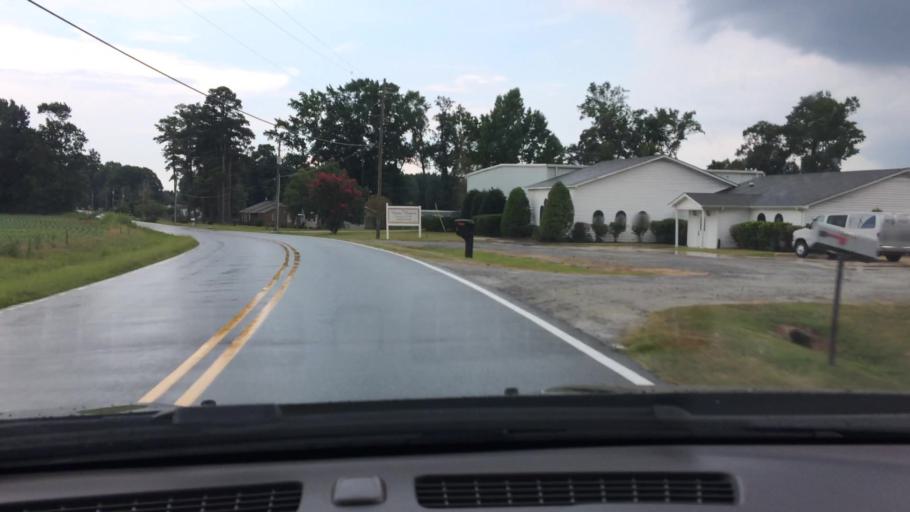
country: US
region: North Carolina
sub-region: Pitt County
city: Ayden
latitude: 35.4926
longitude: -77.3781
